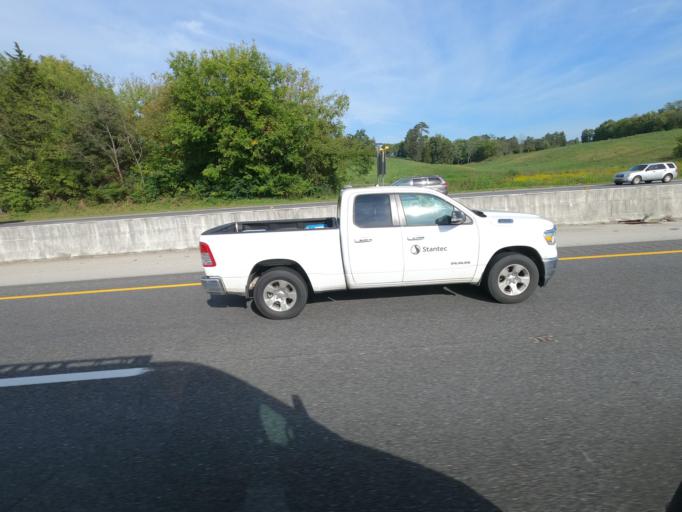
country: US
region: Tennessee
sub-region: Jefferson County
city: Dandridge
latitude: 36.0422
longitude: -83.4311
